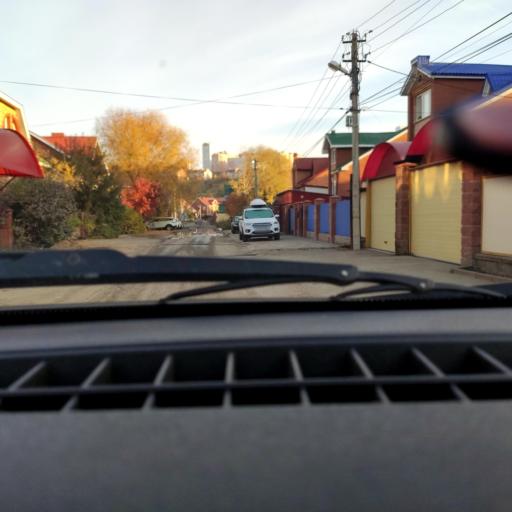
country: RU
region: Bashkortostan
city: Ufa
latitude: 54.6903
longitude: 55.9774
